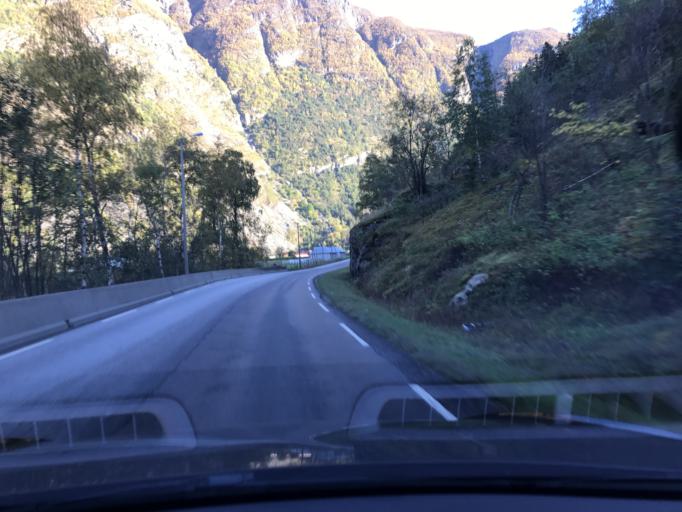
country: NO
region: Sogn og Fjordane
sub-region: Laerdal
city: Laerdalsoyri
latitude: 61.0991
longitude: 7.5129
